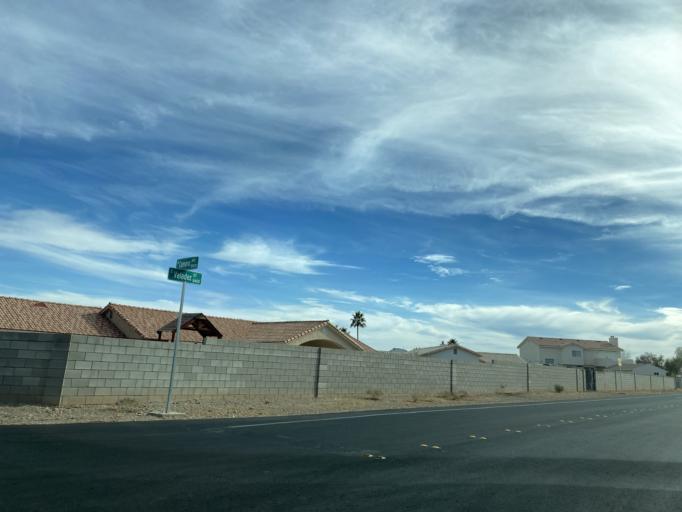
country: US
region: Nevada
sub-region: Clark County
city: Enterprise
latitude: 36.0354
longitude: -115.2678
